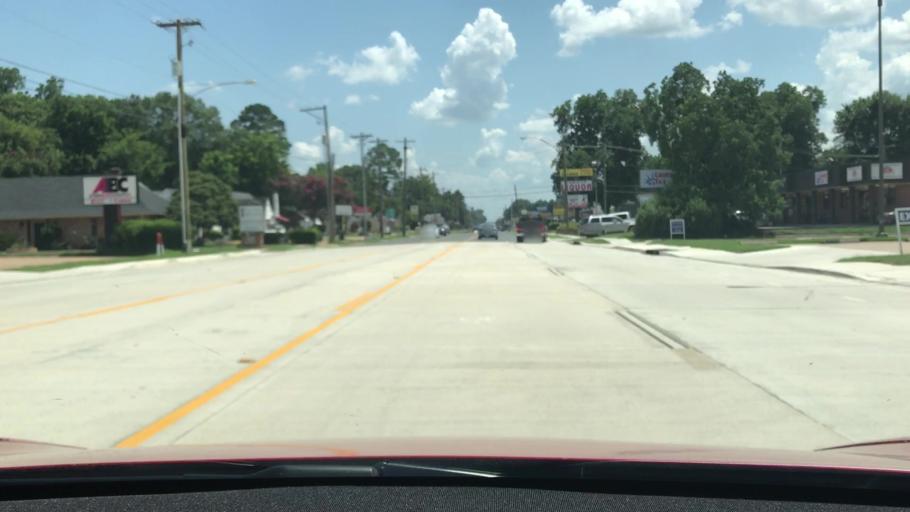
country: US
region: Louisiana
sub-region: Bossier Parish
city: Bossier City
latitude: 32.4777
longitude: -93.7222
